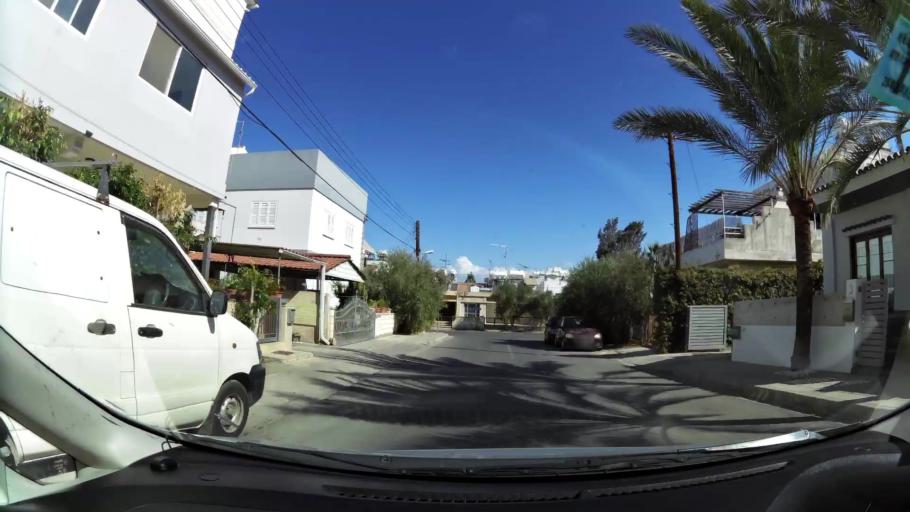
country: CY
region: Lefkosia
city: Nicosia
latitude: 35.1366
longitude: 33.3438
